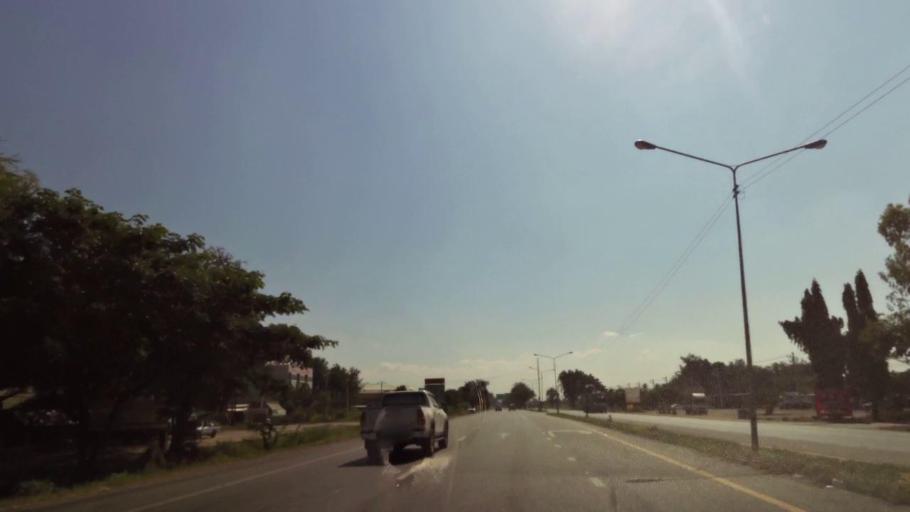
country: TH
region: Nakhon Sawan
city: Nakhon Sawan
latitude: 15.7752
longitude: 100.1214
